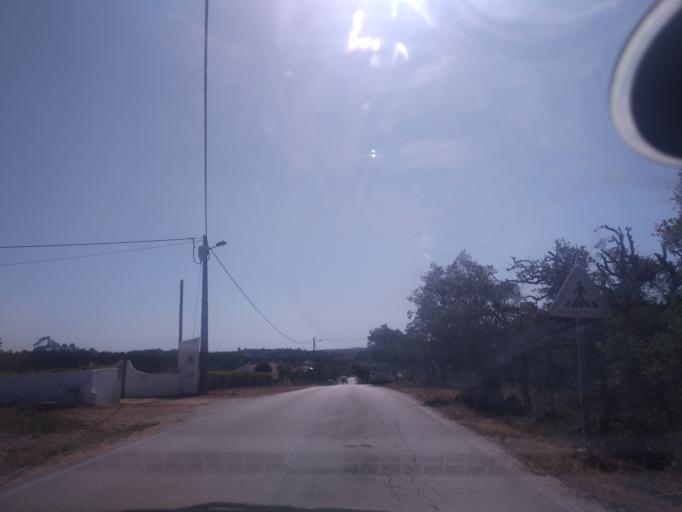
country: PT
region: Faro
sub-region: Aljezur
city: Aljezur
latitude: 37.2276
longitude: -8.8177
